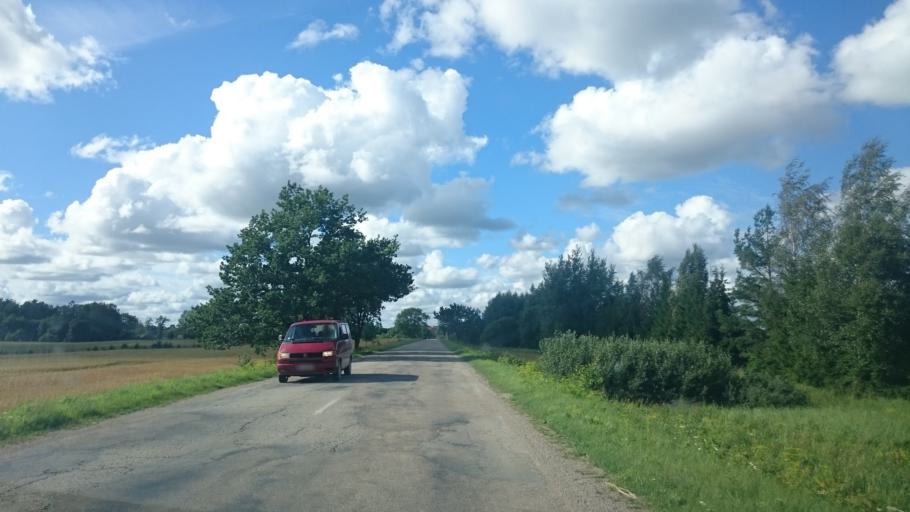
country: LV
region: Aizpute
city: Aizpute
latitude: 56.7008
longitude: 21.6288
